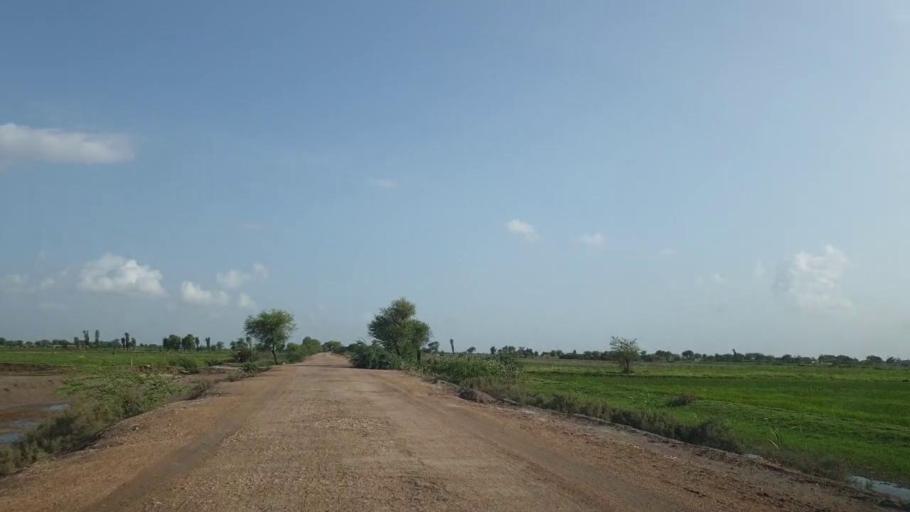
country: PK
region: Sindh
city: Kadhan
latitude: 24.6315
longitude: 69.0959
